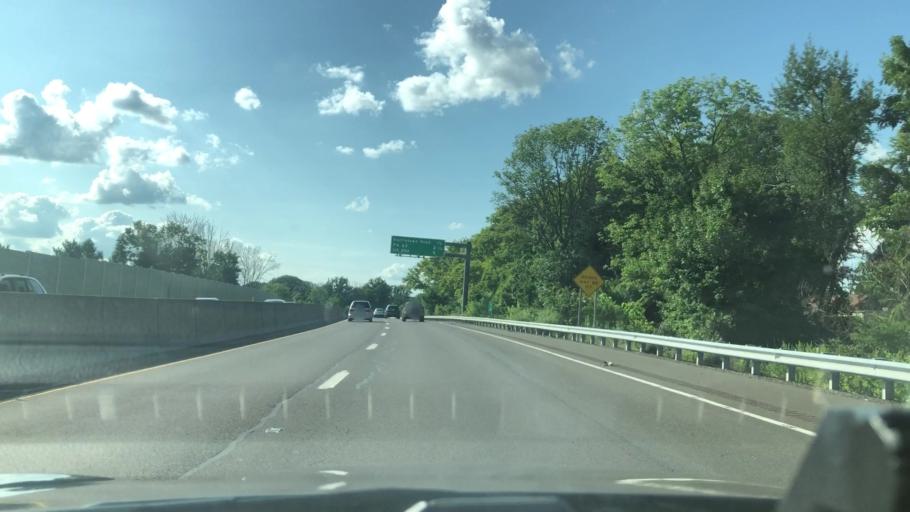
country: US
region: Pennsylvania
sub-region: Montgomery County
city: Ambler
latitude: 40.1713
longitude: -75.2089
